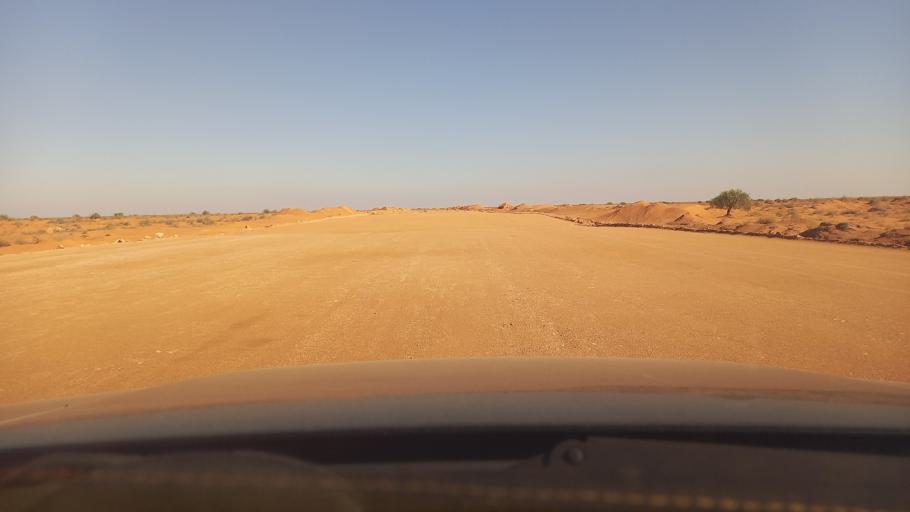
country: TN
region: Madanin
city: Medenine
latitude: 33.1595
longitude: 10.5177
